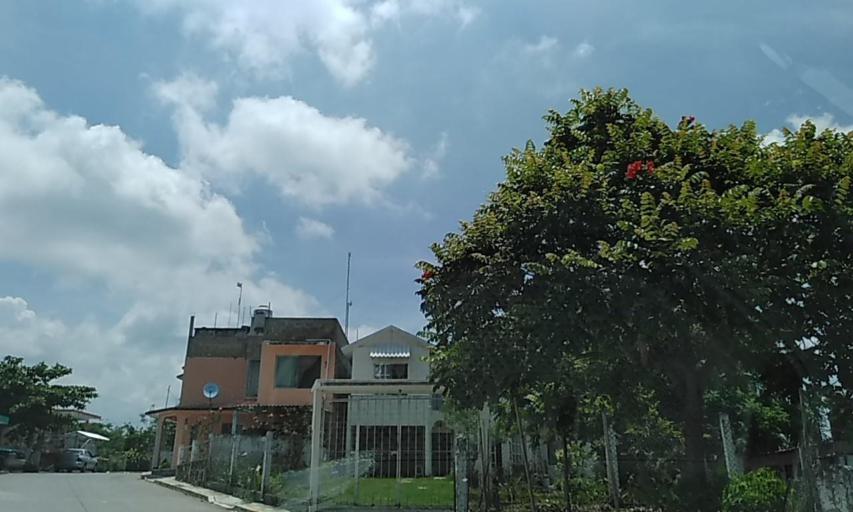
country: MX
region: Veracruz
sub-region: Emiliano Zapata
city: Dos Rios
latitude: 19.4419
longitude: -96.7552
